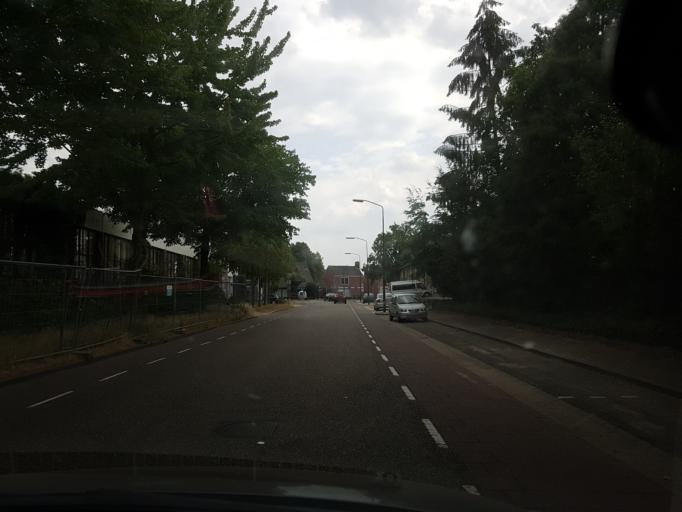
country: NL
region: North Brabant
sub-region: Gemeente Geldrop-Mierlo
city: Geldrop
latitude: 51.4279
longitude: 5.5661
